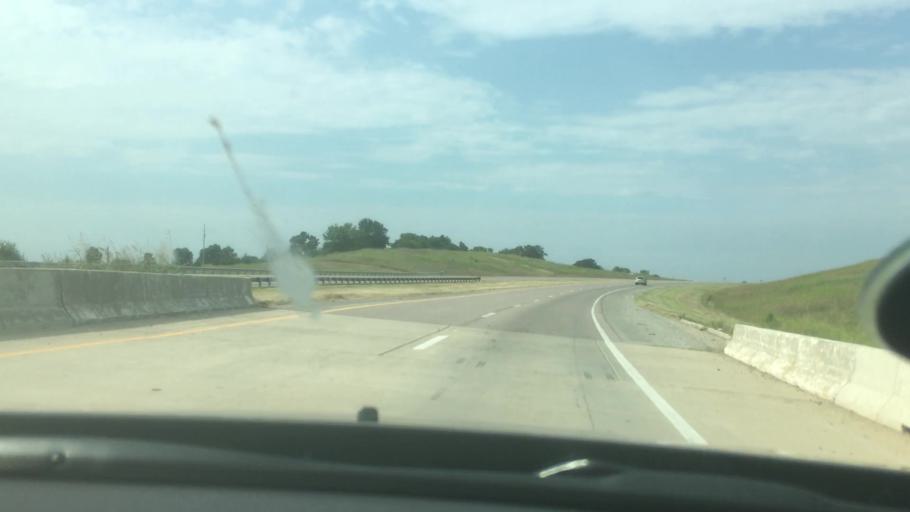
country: US
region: Oklahoma
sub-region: Pontotoc County
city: Ada
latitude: 34.8112
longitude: -96.6960
